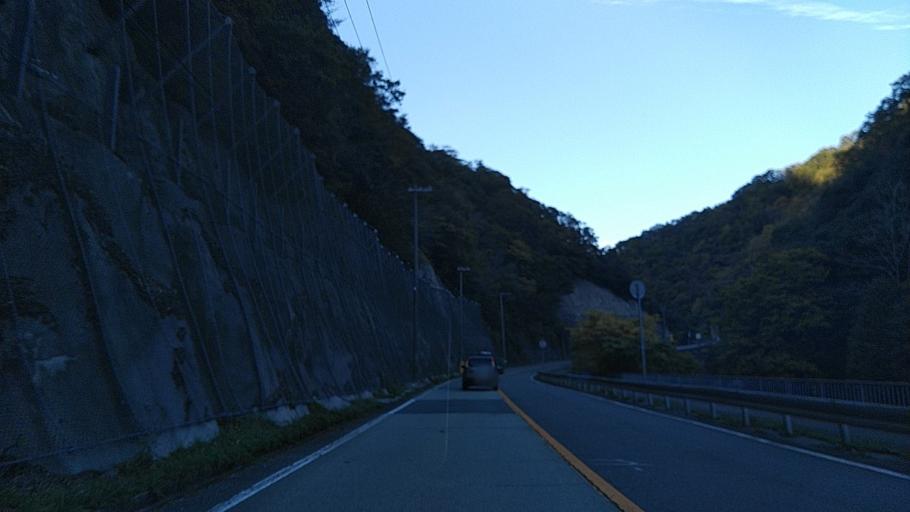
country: JP
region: Osaka
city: Ikeda
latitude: 34.9376
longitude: 135.4087
